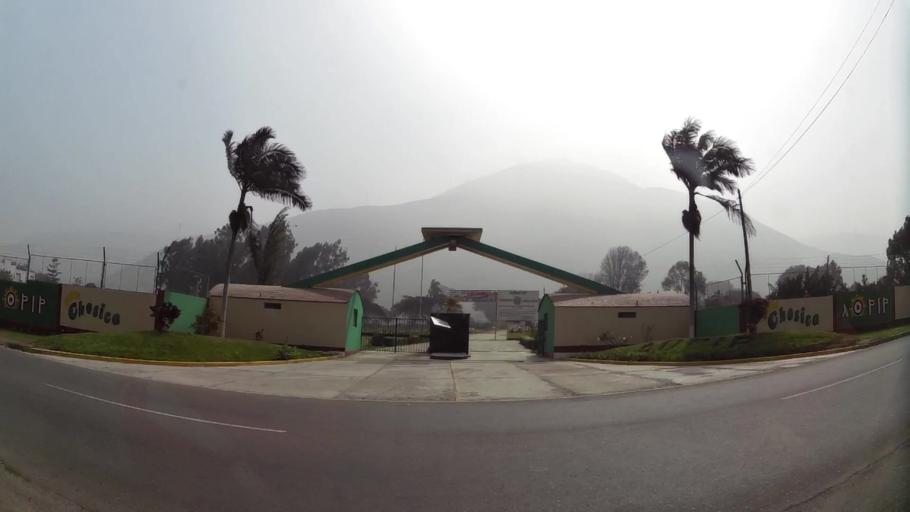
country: PE
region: Lima
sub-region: Lima
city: Chosica
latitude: -11.9601
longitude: -76.7364
